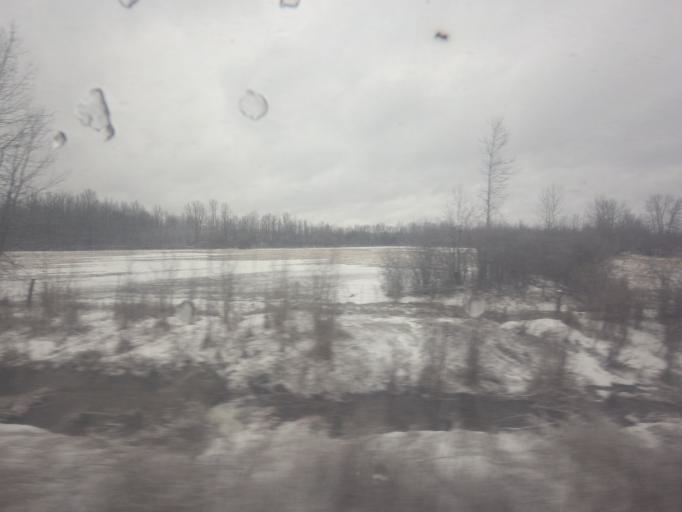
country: CA
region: Ontario
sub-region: Lanark County
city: Smiths Falls
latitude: 44.9305
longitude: -76.0269
